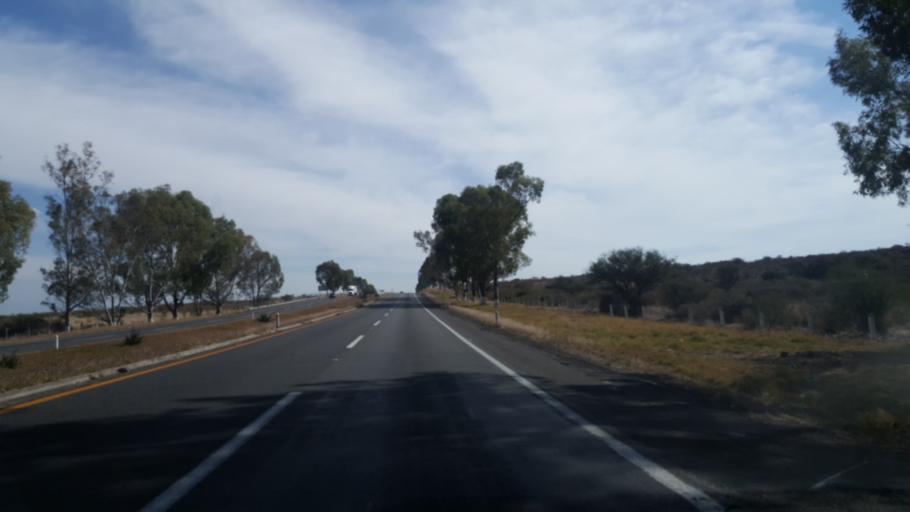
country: MX
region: Jalisco
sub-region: Lagos de Moreno
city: Cristeros [Fraccionamiento]
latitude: 21.2590
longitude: -101.9554
